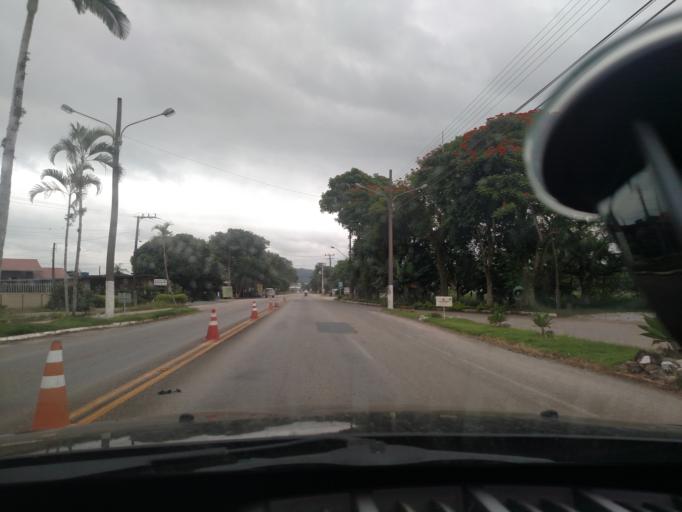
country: BR
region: Santa Catarina
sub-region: Gaspar
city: Gaspar
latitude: -26.9195
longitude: -48.9021
